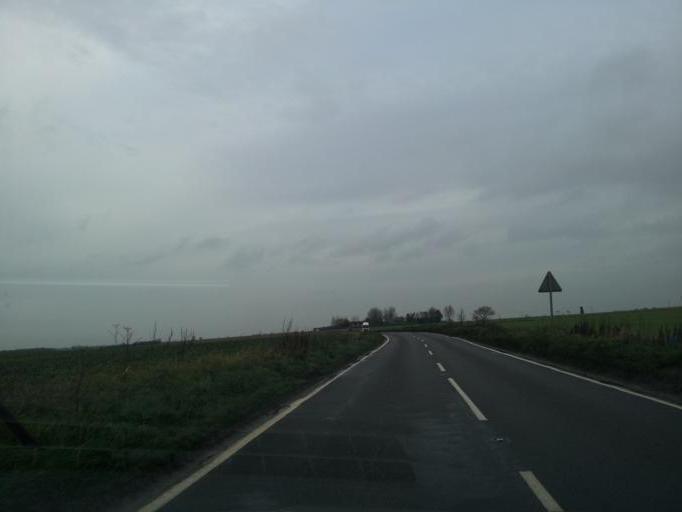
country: GB
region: England
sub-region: Norfolk
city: Martham
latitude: 52.6799
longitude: 1.5945
